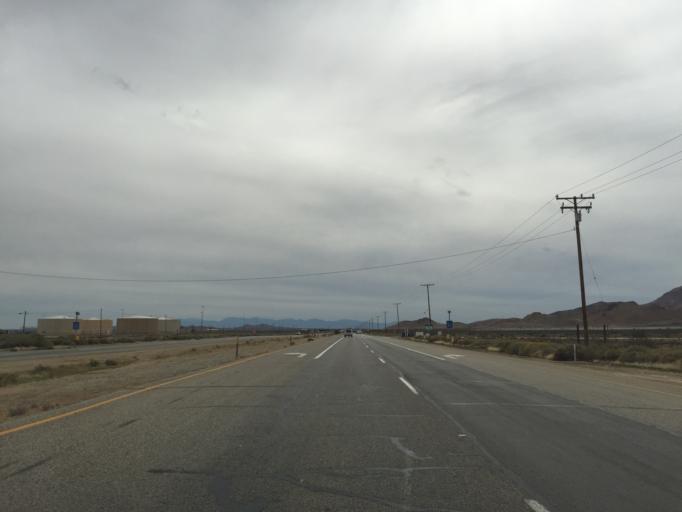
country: US
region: California
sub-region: Kern County
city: Mojave
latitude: 35.0339
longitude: -118.1690
